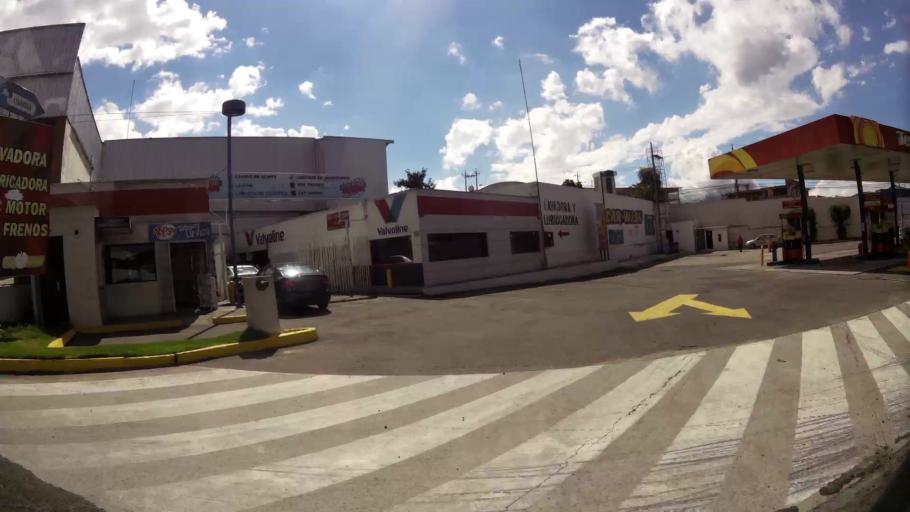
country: EC
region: Pichincha
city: Quito
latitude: -0.1054
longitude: -78.4720
